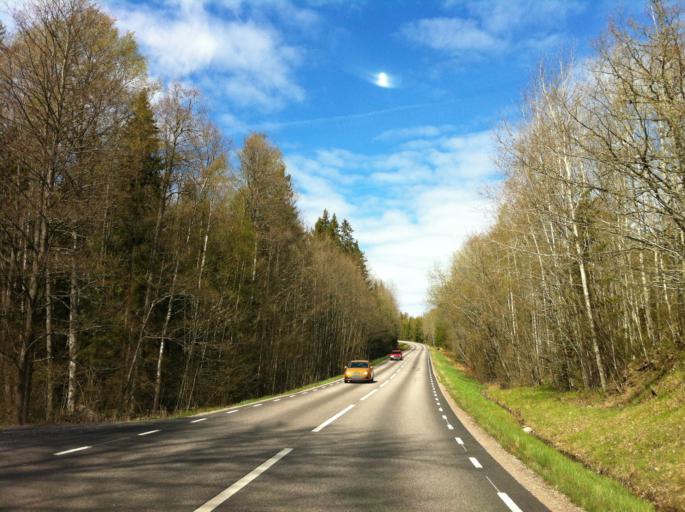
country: SE
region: Kalmar
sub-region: Vasterviks Kommun
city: Forserum
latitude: 58.0760
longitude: 16.5177
